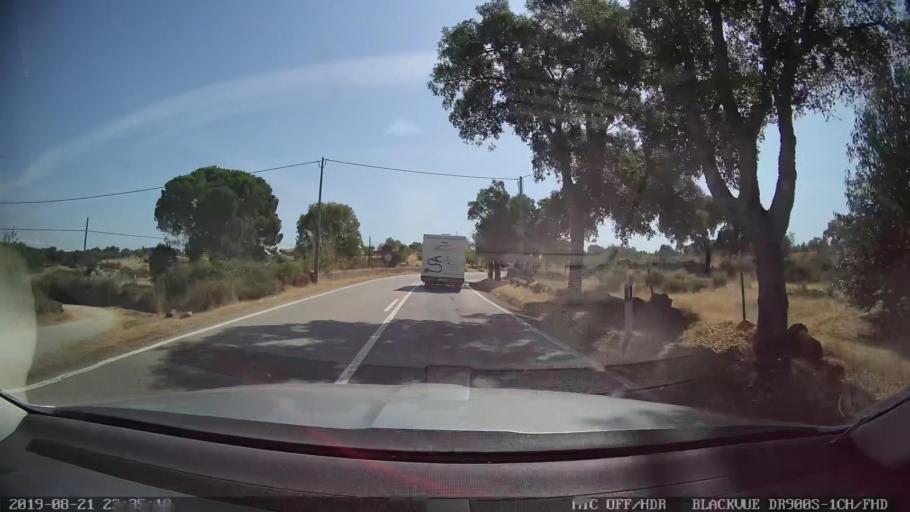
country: PT
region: Guarda
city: Alcains
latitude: 39.8787
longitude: -7.3895
